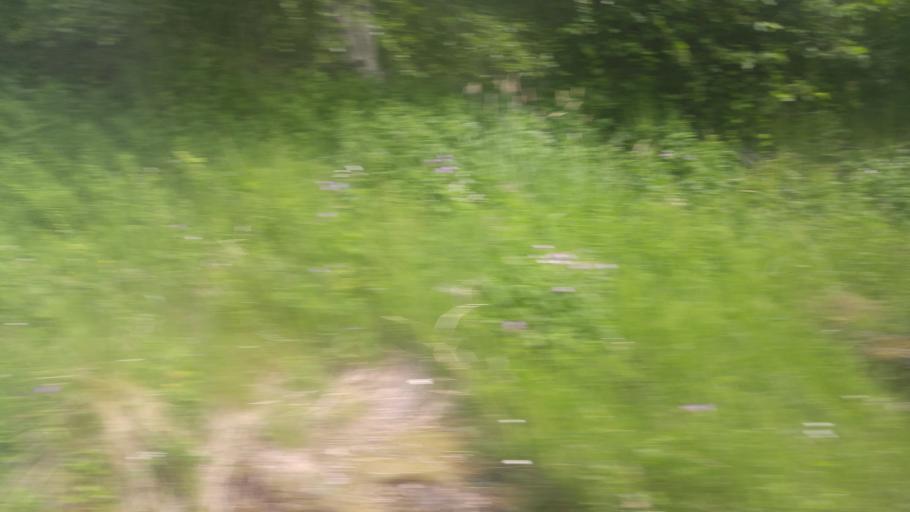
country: NO
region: Sor-Trondelag
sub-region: Midtre Gauldal
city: Storen
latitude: 62.9435
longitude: 10.6564
